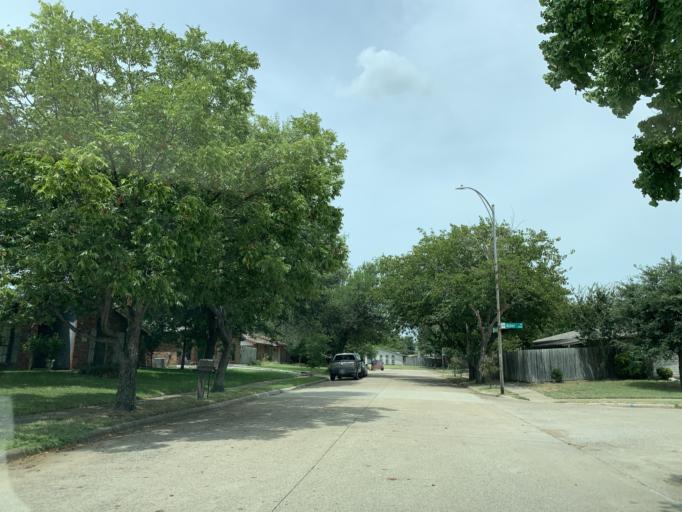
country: US
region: Texas
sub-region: Dallas County
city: Grand Prairie
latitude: 32.6539
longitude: -97.0345
